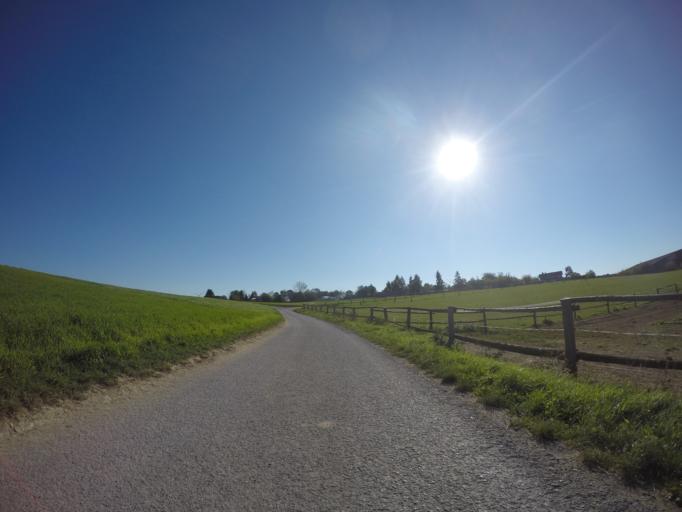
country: DE
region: Bavaria
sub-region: Regierungsbezirk Unterfranken
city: Remlingen
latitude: 49.8096
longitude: 9.6900
